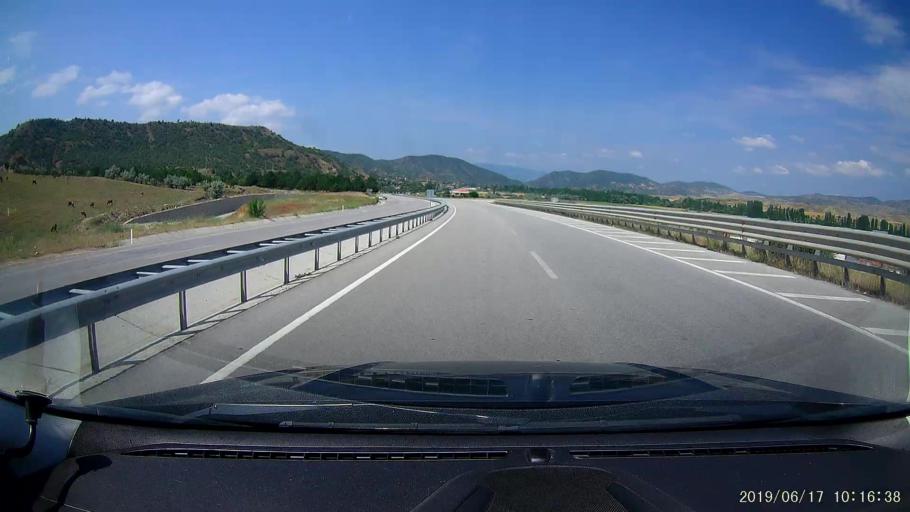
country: TR
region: Corum
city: Osmancik
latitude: 40.9882
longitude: 34.9706
